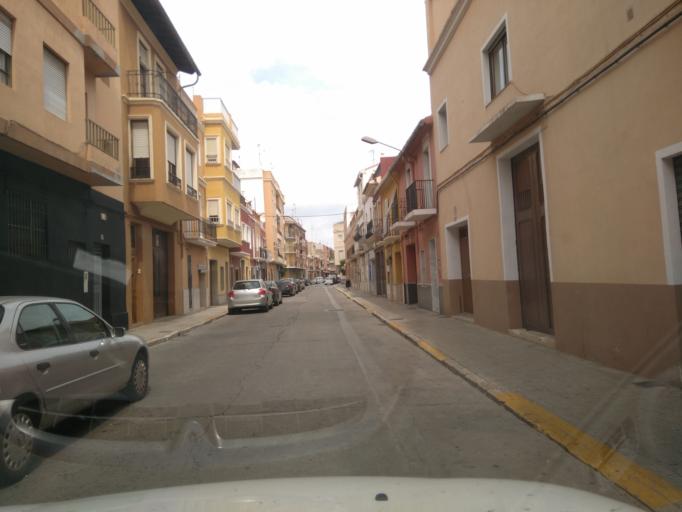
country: ES
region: Valencia
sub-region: Provincia de Valencia
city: Carcaixent
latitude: 39.1233
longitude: -0.4470
